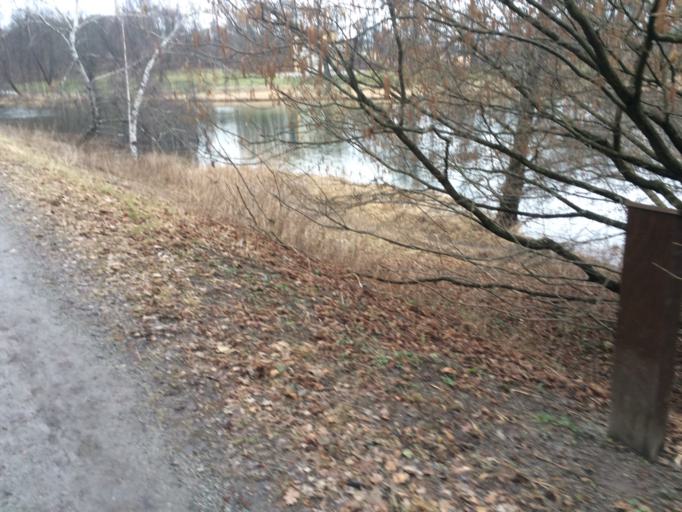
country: SE
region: Stockholm
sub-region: Norrtalje Kommun
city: Bergshamra
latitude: 59.3608
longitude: 18.0389
